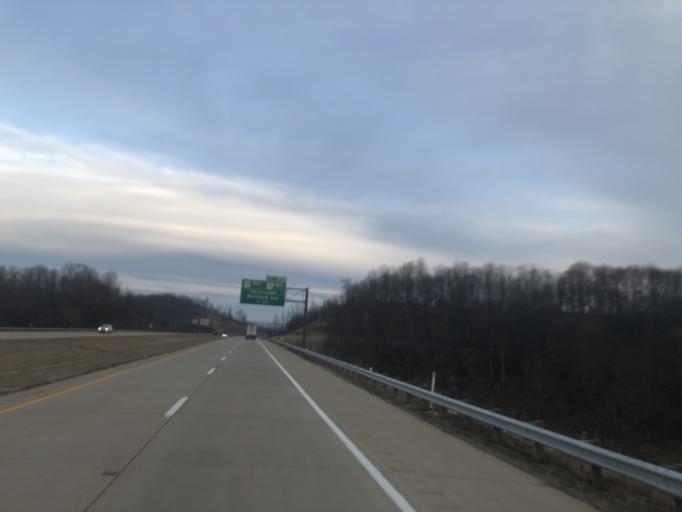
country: US
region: Ohio
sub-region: Athens County
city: Athens
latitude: 39.2879
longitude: -82.1018
